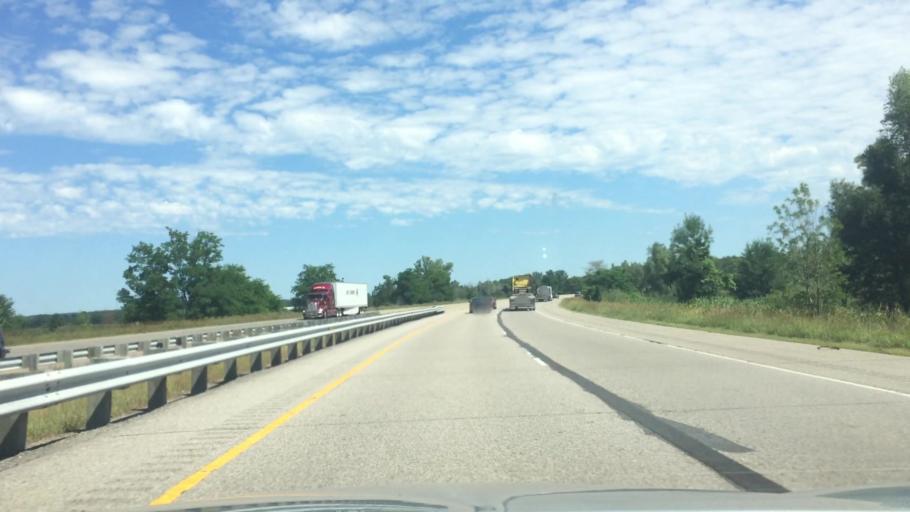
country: US
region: Wisconsin
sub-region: Marquette County
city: Westfield
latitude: 43.7335
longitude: -89.4848
